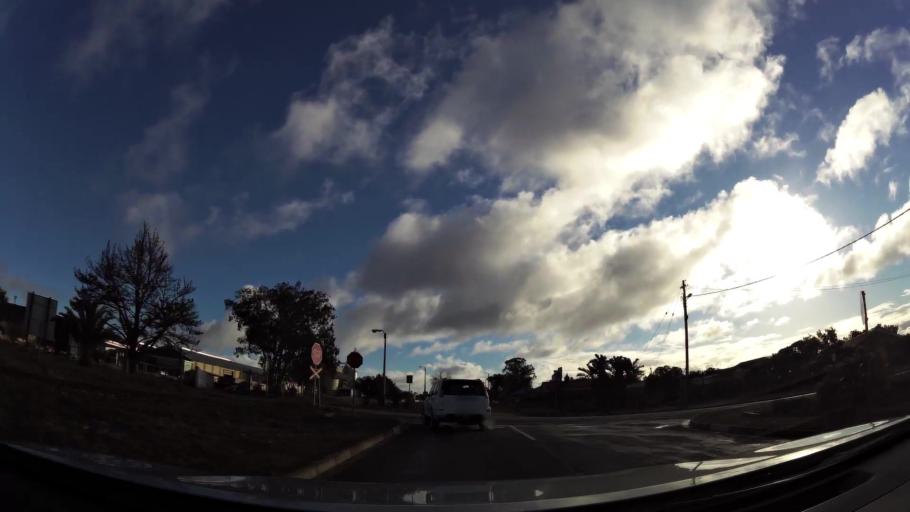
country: ZA
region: Western Cape
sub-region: Eden District Municipality
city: Riversdale
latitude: -34.2093
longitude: 21.5850
